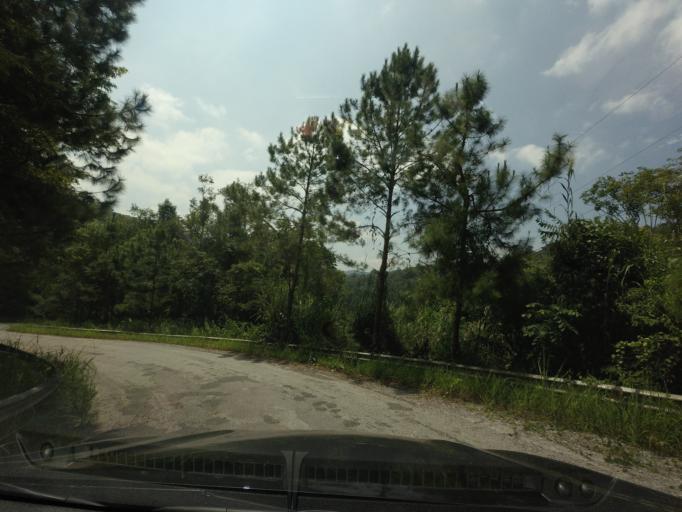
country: TH
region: Loei
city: Na Haeo
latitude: 17.4876
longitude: 100.9393
